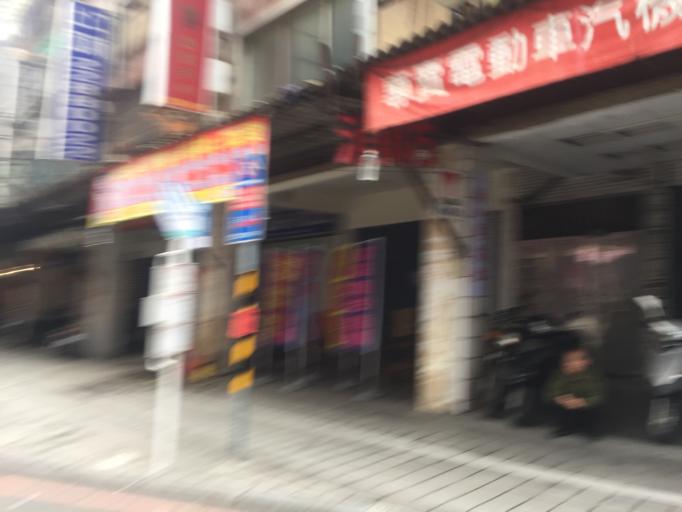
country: TW
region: Taipei
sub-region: Taipei
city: Banqiao
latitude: 25.0889
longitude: 121.4692
